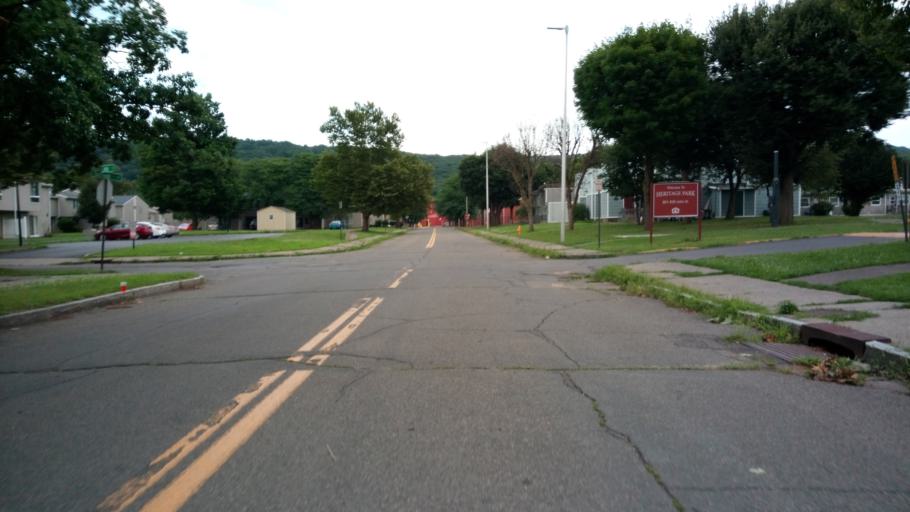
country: US
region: New York
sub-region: Chemung County
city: Elmira
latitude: 42.0911
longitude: -76.7927
